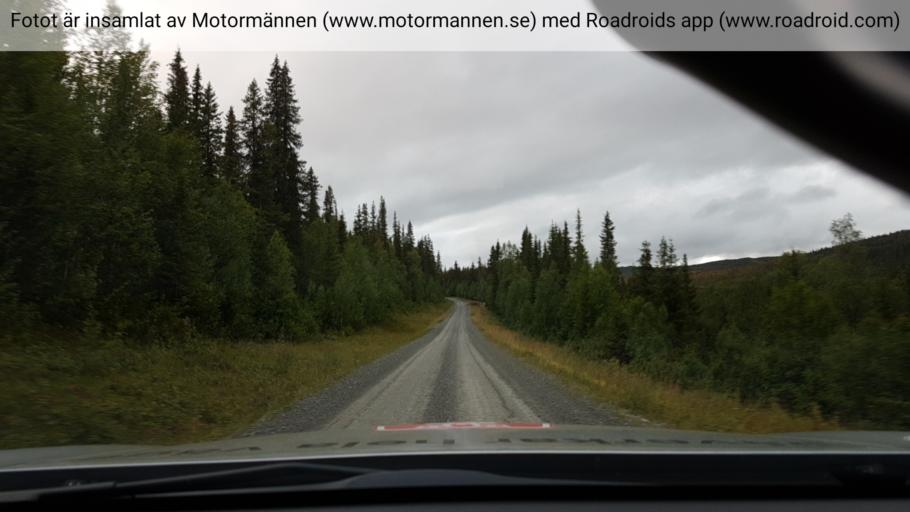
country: SE
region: Vaesterbotten
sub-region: Vilhelmina Kommun
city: Sjoberg
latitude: 65.5356
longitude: 15.4333
